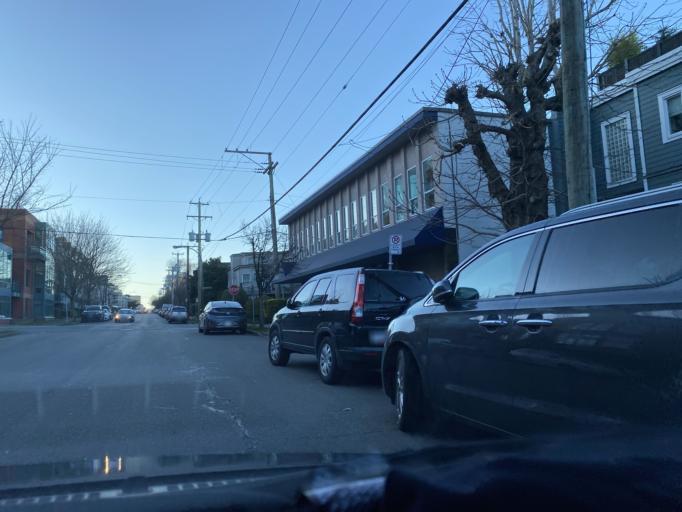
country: CA
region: British Columbia
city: Vancouver
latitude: 49.2644
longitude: -123.1283
